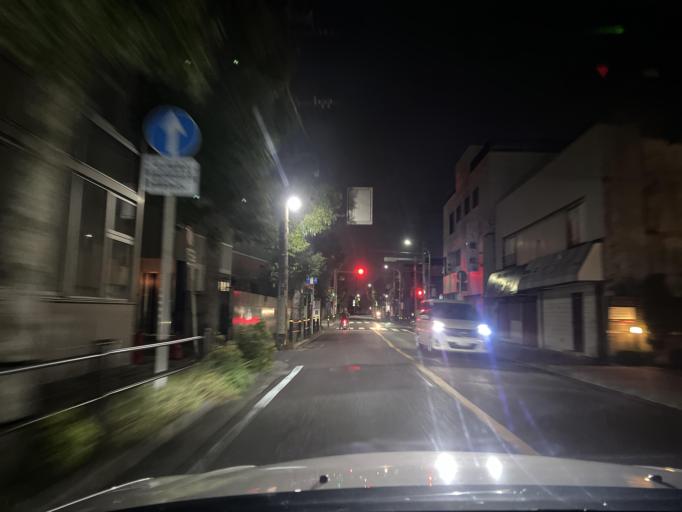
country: JP
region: Chiba
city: Funabashi
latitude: 35.7268
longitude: 139.9330
